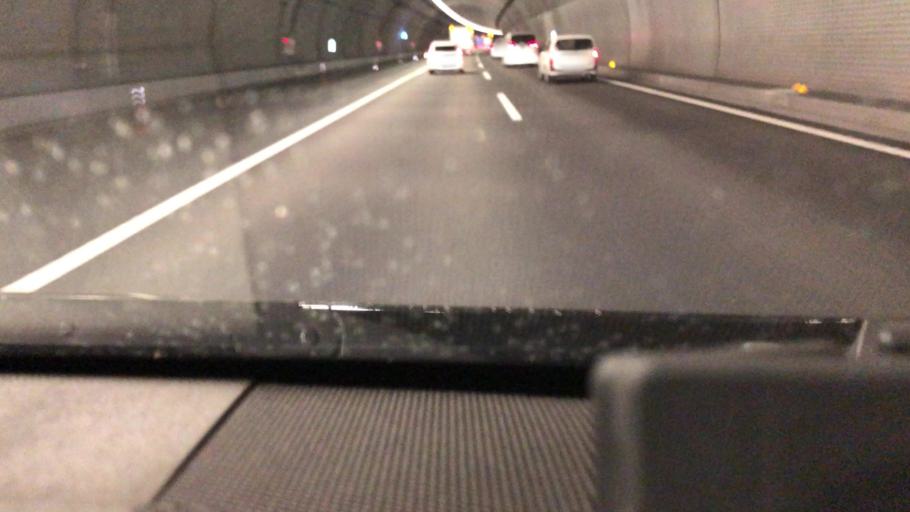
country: JP
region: Shizuoka
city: Shizuoka-shi
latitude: 35.0571
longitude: 138.4271
